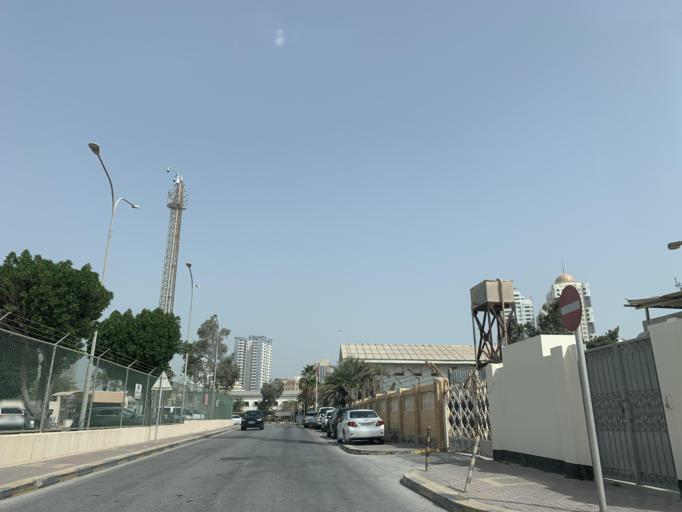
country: BH
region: Manama
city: Manama
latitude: 26.2081
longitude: 50.6056
